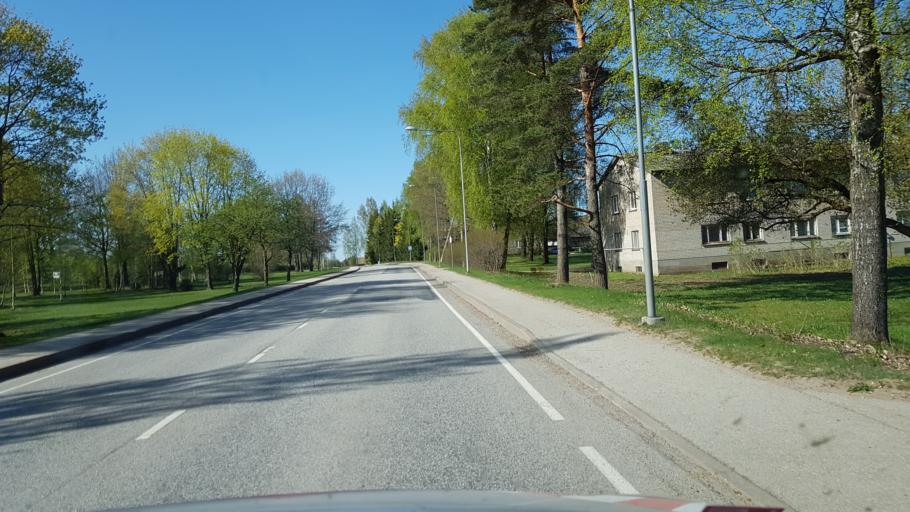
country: EE
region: Viljandimaa
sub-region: Abja vald
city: Abja-Paluoja
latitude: 58.1220
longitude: 25.3637
